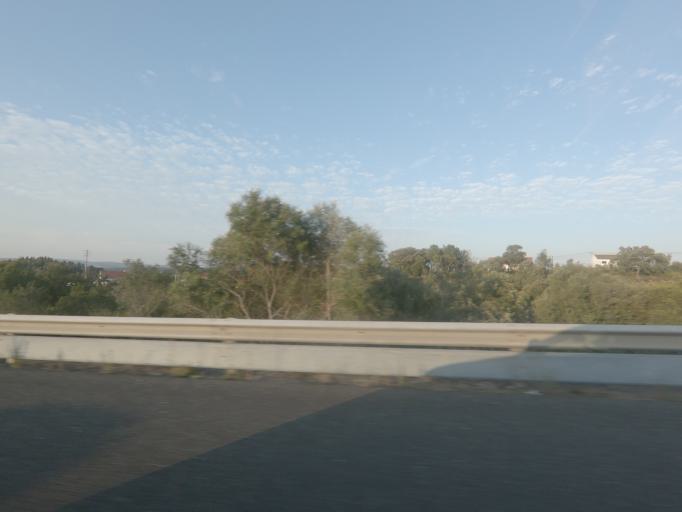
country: PT
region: Leiria
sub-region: Leiria
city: Santa Catarina da Serra
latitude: 39.6990
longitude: -8.6962
